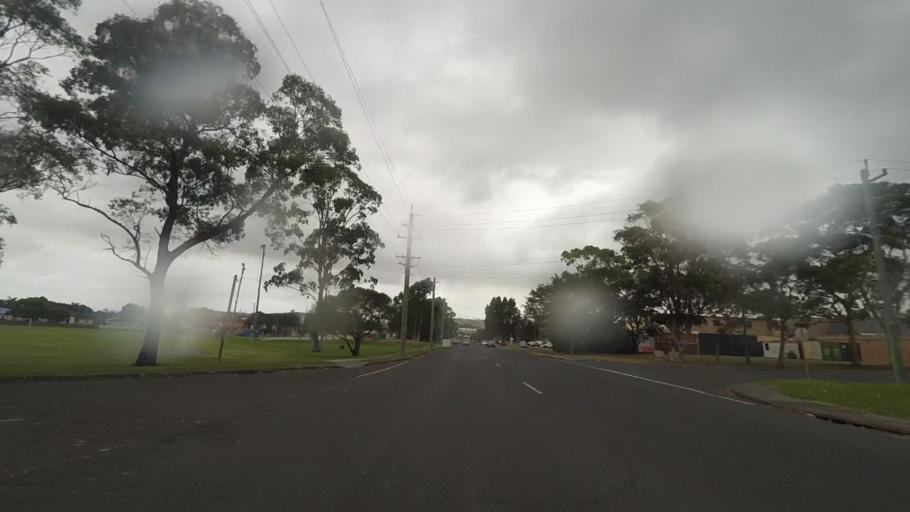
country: AU
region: New South Wales
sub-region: Wollongong
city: Cordeaux Heights
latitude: -34.4504
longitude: 150.8434
